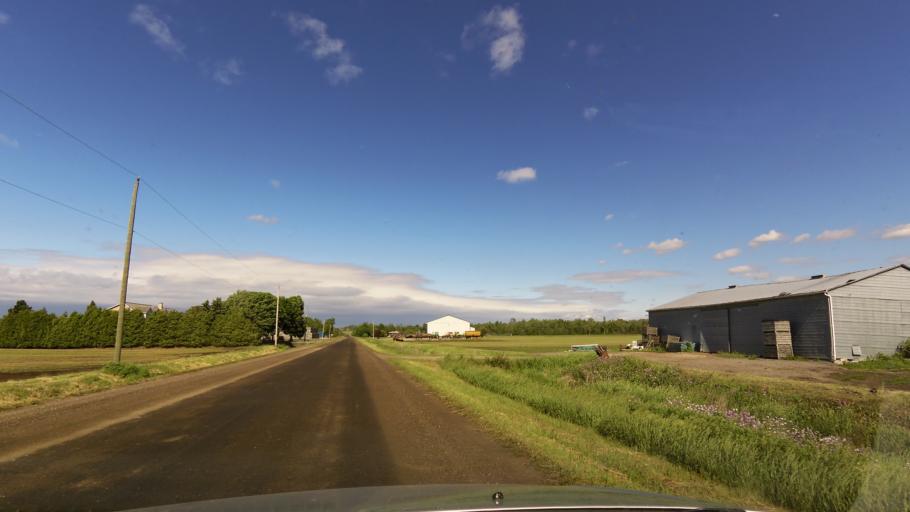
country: CA
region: Ontario
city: Innisfil
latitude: 44.2323
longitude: -79.6285
